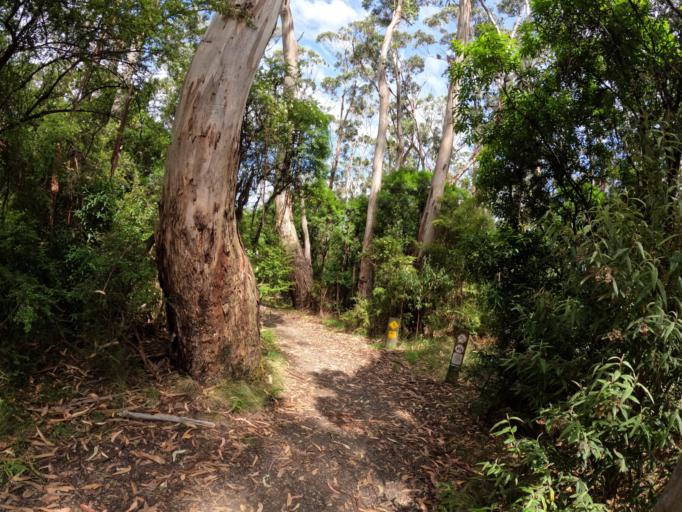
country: AU
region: Victoria
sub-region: Colac-Otway
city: Apollo Bay
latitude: -38.7903
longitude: 143.6194
